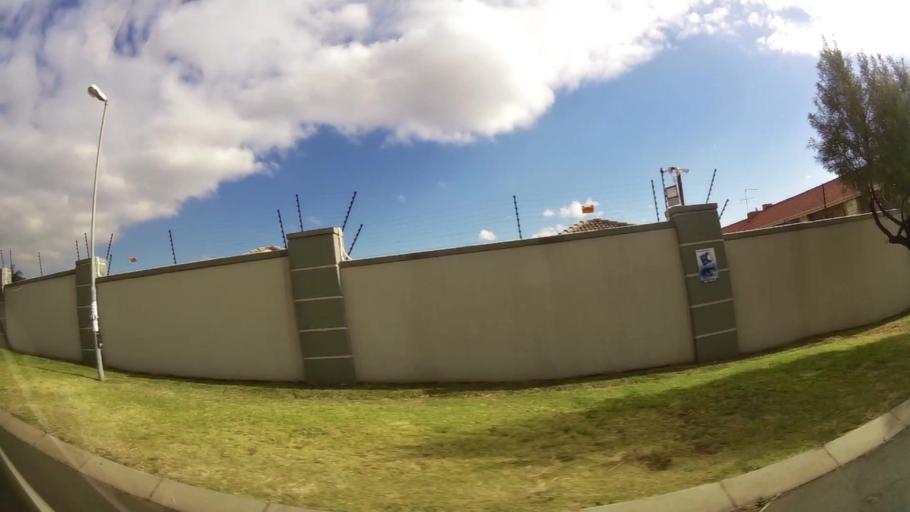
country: ZA
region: Gauteng
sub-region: City of Johannesburg Metropolitan Municipality
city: Roodepoort
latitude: -26.0966
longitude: 27.8725
